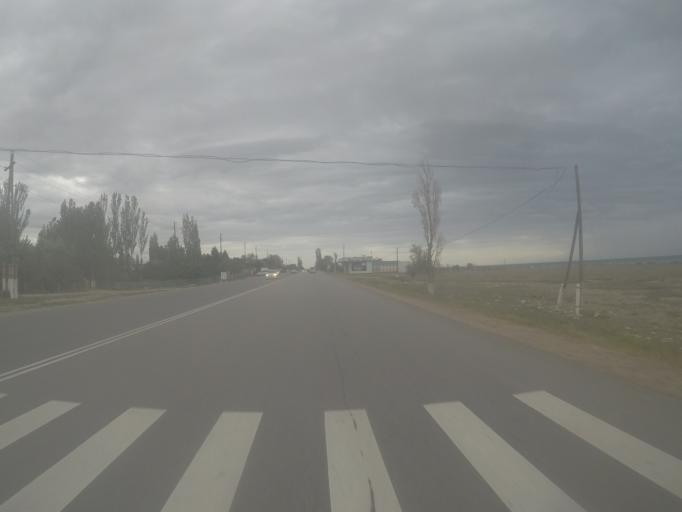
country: KG
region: Ysyk-Koel
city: Cholpon-Ata
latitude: 42.5977
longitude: 76.8588
